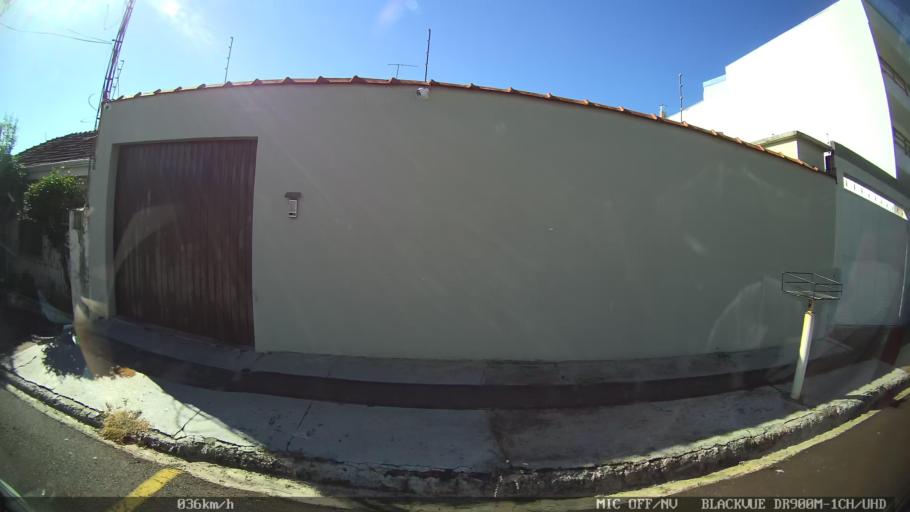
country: BR
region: Sao Paulo
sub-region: Franca
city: Franca
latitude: -20.5323
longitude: -47.4080
